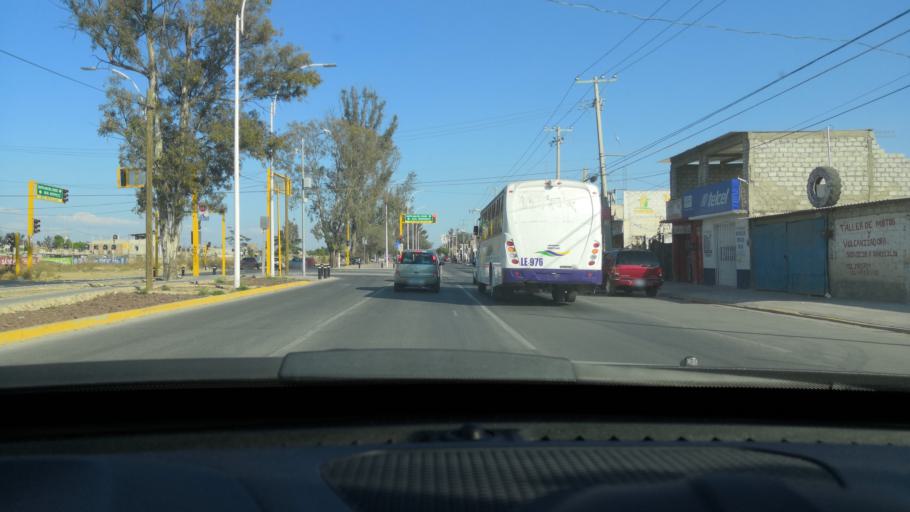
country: MX
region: Guanajuato
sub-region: Leon
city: San Jose de Duran (Los Troncoso)
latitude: 21.0613
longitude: -101.6179
